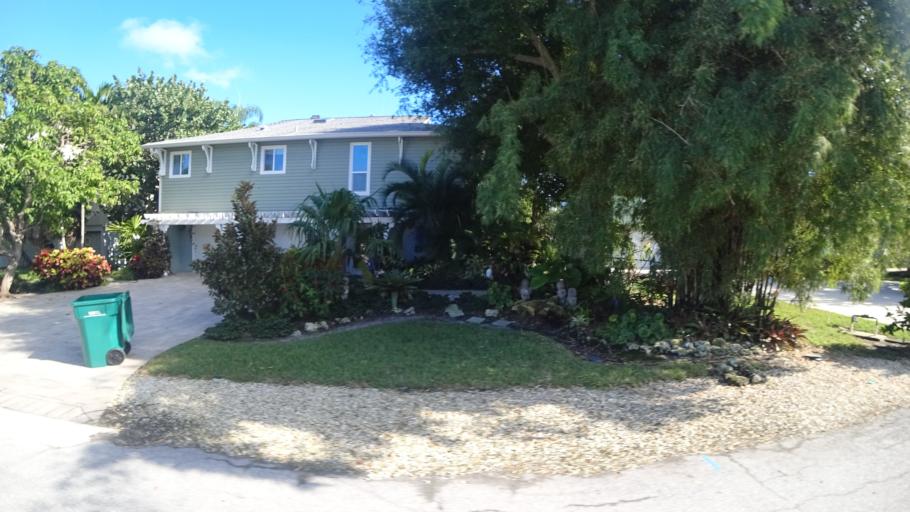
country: US
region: Florida
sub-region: Manatee County
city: Anna Maria
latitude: 27.5298
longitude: -82.7290
